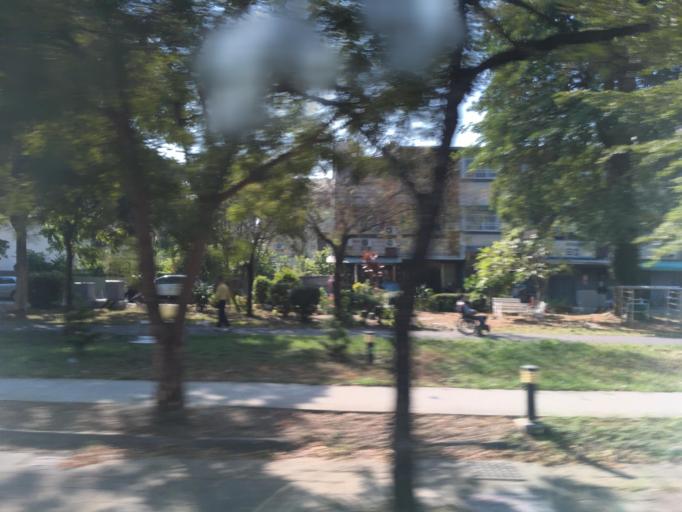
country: TW
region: Taiwan
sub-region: Chiayi
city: Jiayi Shi
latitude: 23.4947
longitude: 120.4405
